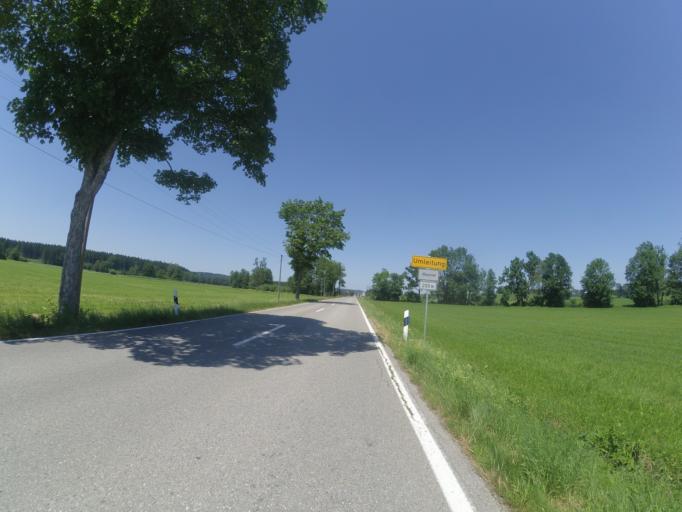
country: DE
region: Bavaria
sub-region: Swabia
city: Bohen
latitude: 47.8966
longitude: 10.3209
